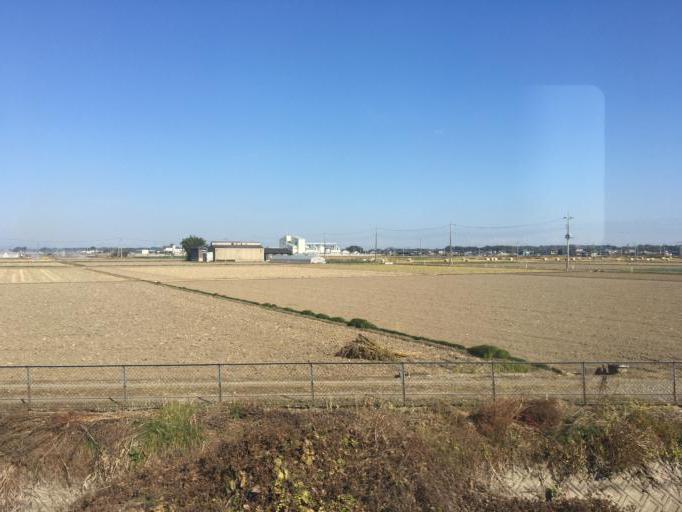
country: JP
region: Tochigi
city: Oyama
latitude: 36.3463
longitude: 139.7902
